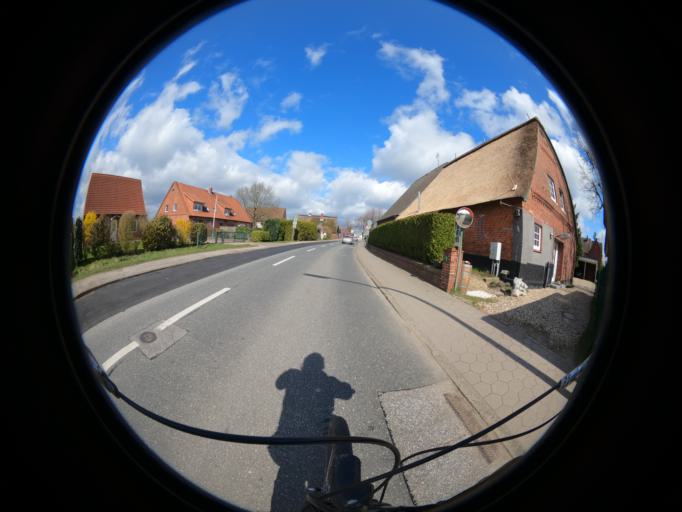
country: DE
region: Lower Saxony
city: Neu Wulmstorf
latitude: 53.5145
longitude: 9.7926
